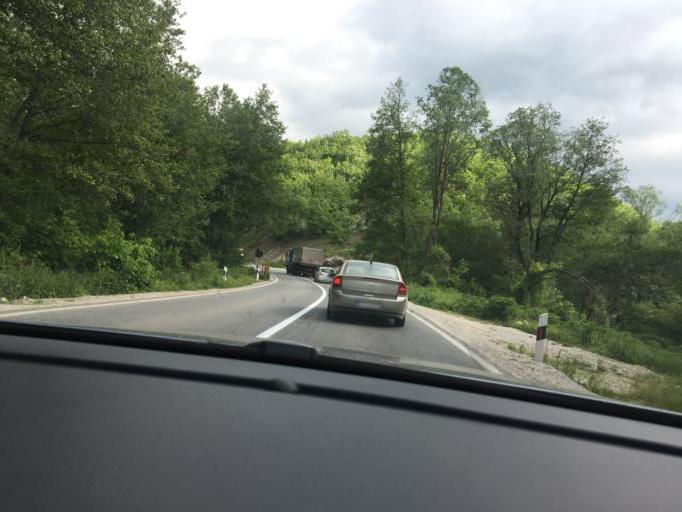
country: MK
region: Resen
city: Jankovec
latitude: 41.1416
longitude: 21.0003
